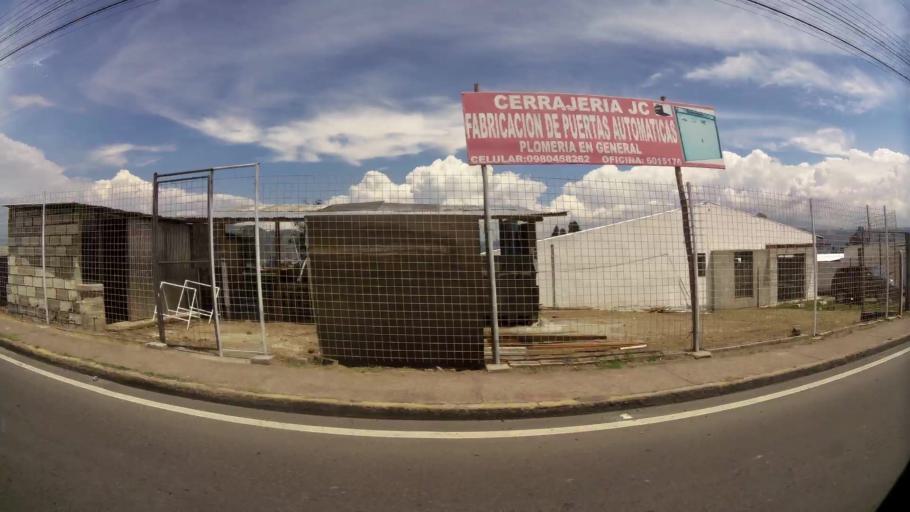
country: EC
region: Pichincha
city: Sangolqui
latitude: -0.2049
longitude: -78.3677
